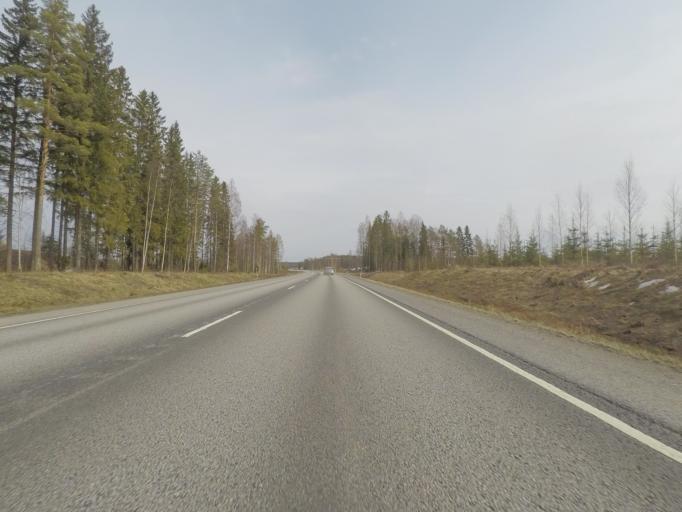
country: FI
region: Central Finland
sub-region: Jyvaeskylae
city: Toivakka
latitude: 62.2512
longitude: 26.2287
